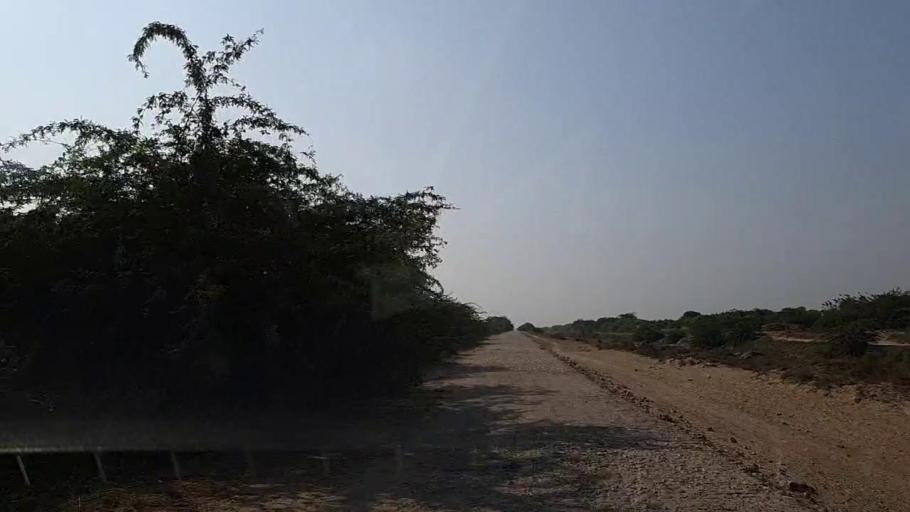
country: PK
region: Sindh
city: Mirpur Sakro
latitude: 24.6373
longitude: 67.7360
